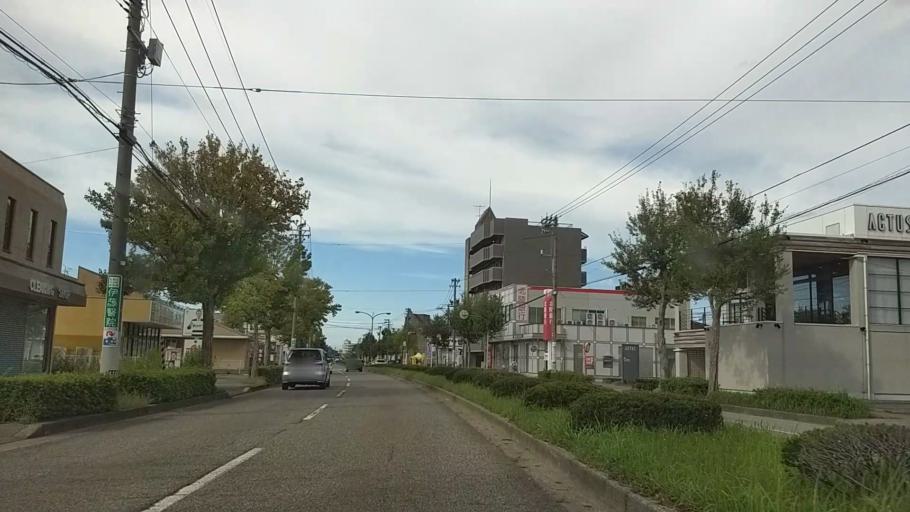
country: JP
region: Ishikawa
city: Nonoichi
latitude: 36.5355
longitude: 136.6393
